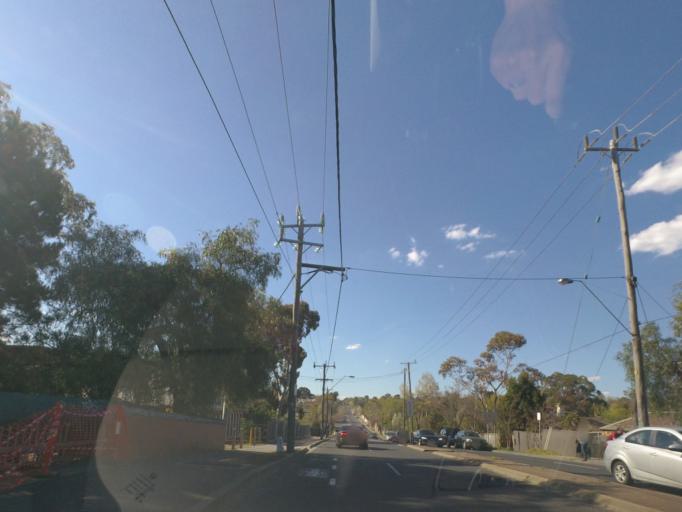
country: AU
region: Victoria
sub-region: Boroondara
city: Kew
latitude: -37.8206
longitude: 145.0265
